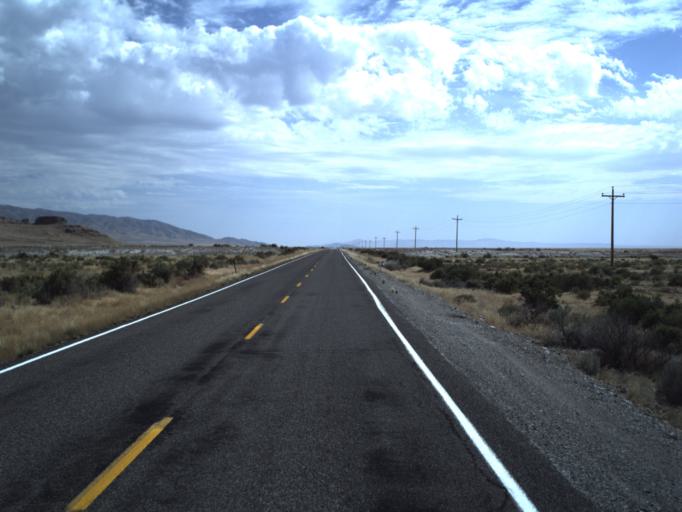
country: US
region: Utah
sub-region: Tooele County
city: Wendover
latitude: 41.4253
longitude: -113.8527
